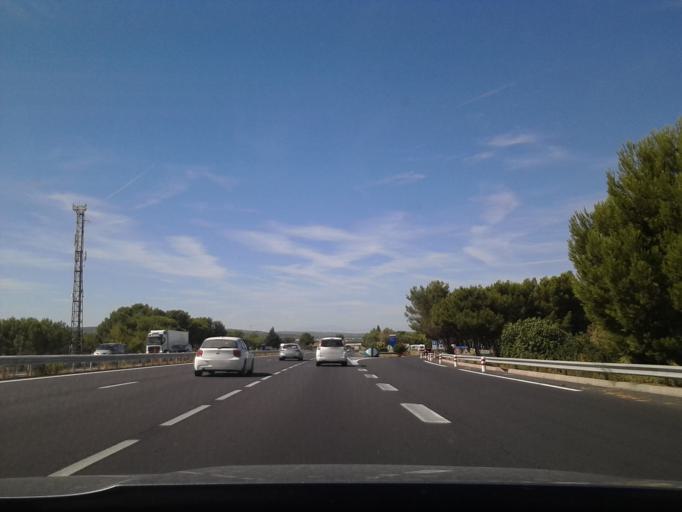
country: FR
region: Languedoc-Roussillon
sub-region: Departement de l'Herault
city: Lespignan
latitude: 43.2672
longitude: 3.1769
